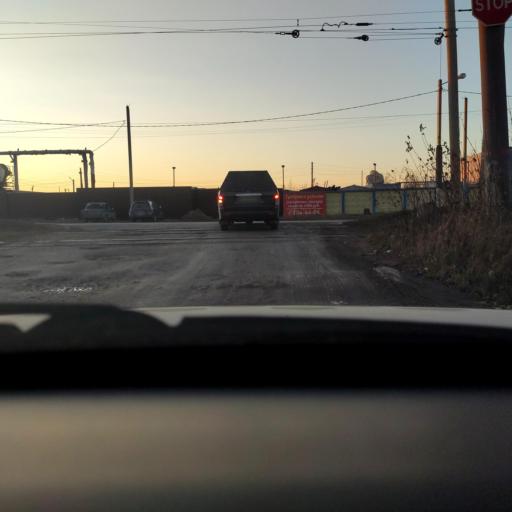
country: RU
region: Perm
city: Kondratovo
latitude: 57.9423
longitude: 56.1260
